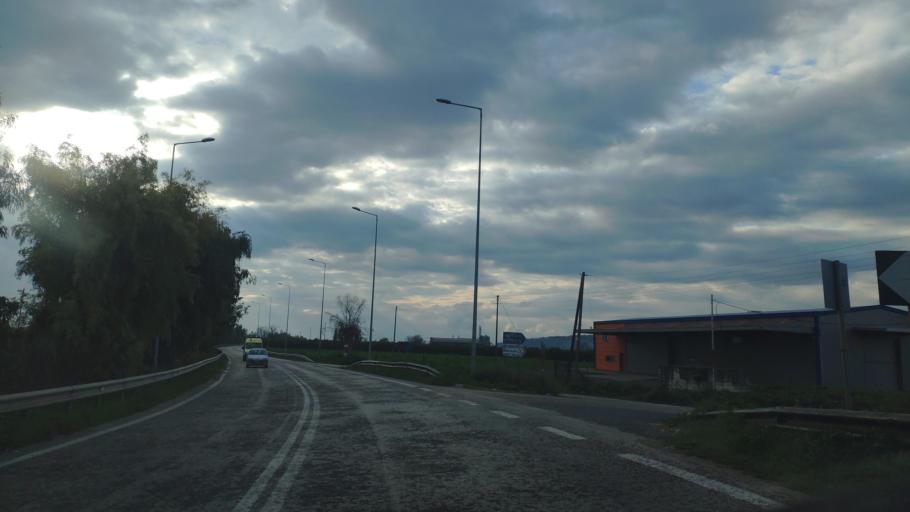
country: GR
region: Peloponnese
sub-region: Nomos Argolidos
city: Koutsopodi
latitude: 37.6713
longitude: 22.7199
